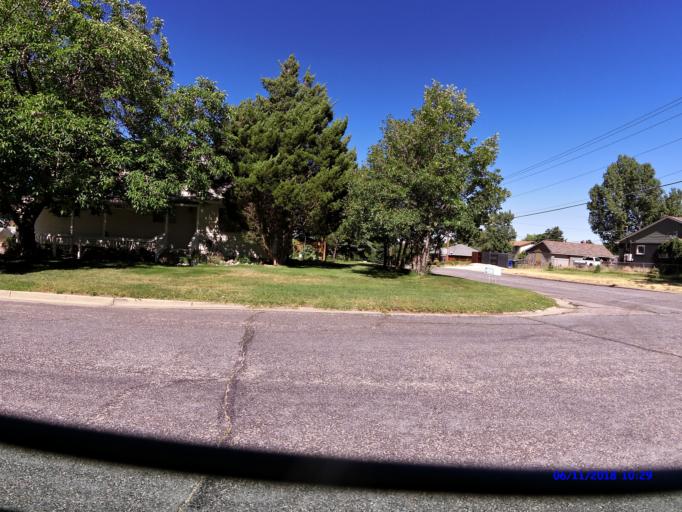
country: US
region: Utah
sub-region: Weber County
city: Ogden
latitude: 41.2285
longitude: -111.9424
